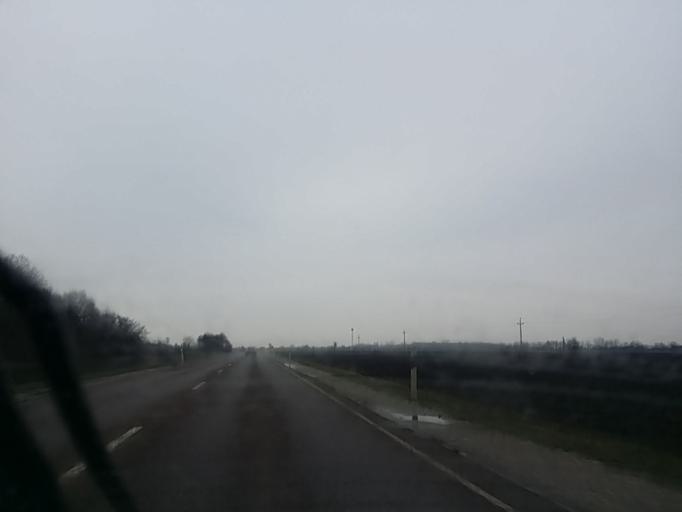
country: HU
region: Borsod-Abauj-Zemplen
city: Mezokeresztes
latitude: 47.8472
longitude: 20.6593
